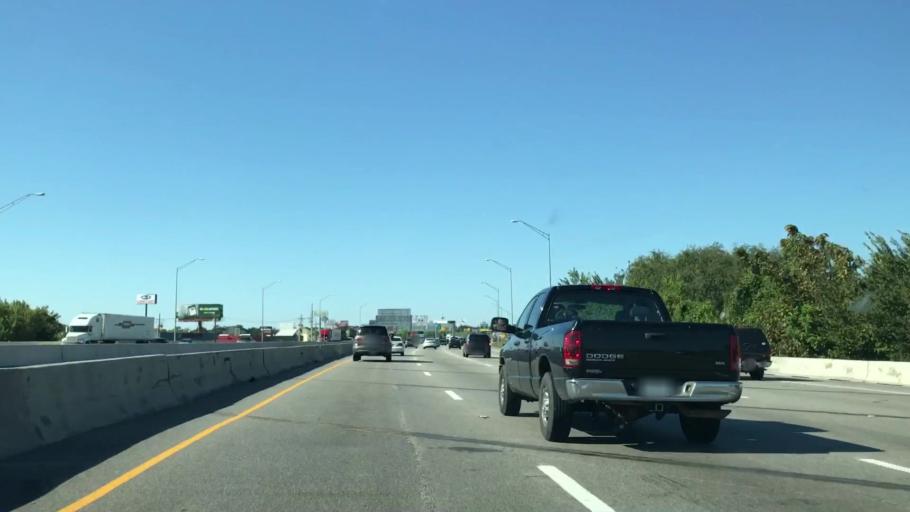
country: US
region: Texas
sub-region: Denton County
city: Lewisville
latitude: 33.0101
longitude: -96.9766
